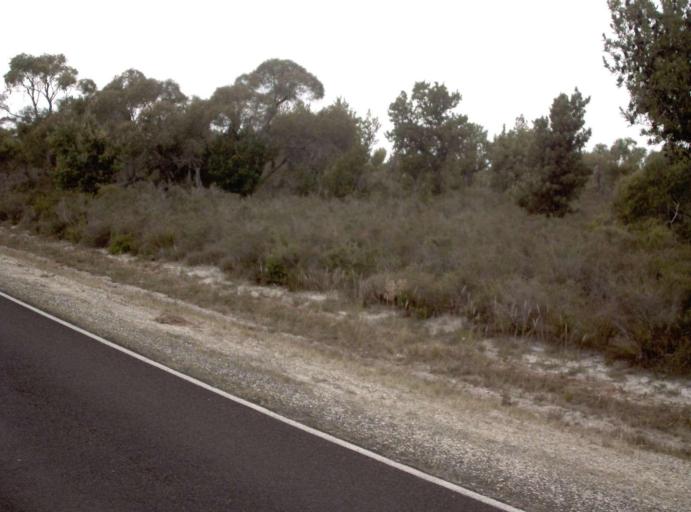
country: AU
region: Victoria
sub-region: East Gippsland
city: Bairnsdale
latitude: -38.1137
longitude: 147.4653
